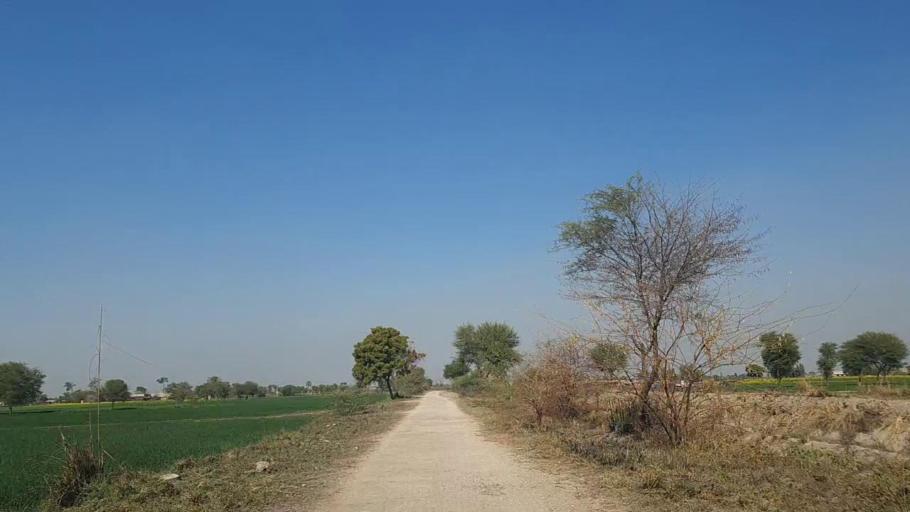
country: PK
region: Sindh
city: Sakrand
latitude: 26.2681
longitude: 68.2210
